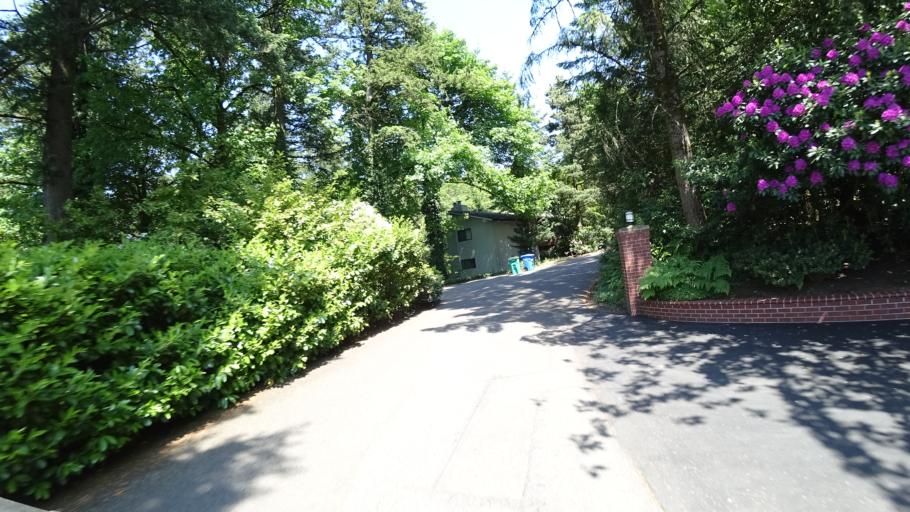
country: US
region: Oregon
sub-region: Washington County
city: West Slope
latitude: 45.5126
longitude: -122.7245
